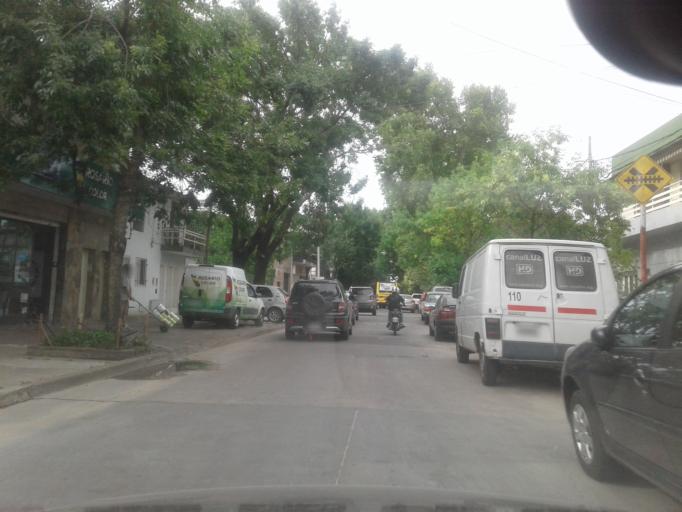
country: AR
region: Santa Fe
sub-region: Departamento de Rosario
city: Rosario
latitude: -32.9689
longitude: -60.6482
